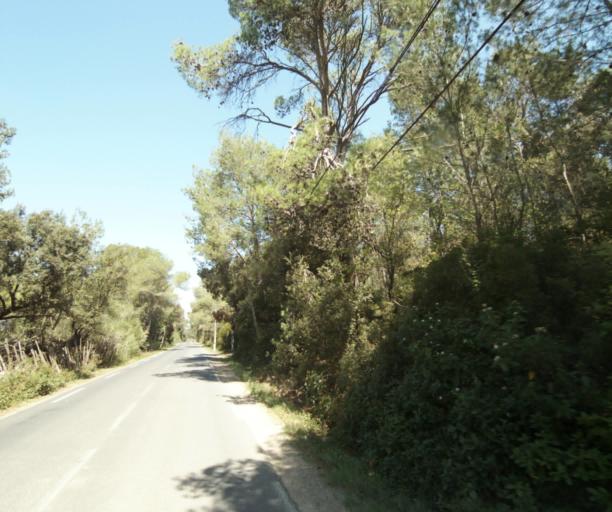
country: FR
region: Languedoc-Roussillon
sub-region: Departement de l'Herault
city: Saint-Genies-des-Mourgues
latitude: 43.6926
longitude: 4.0150
